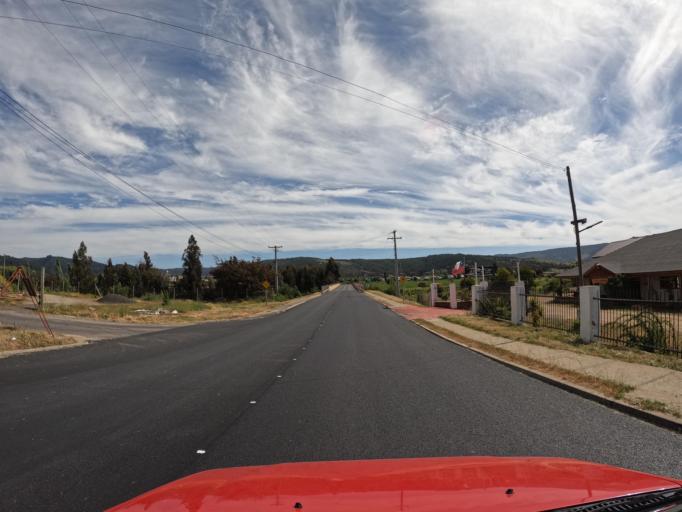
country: CL
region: Maule
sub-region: Provincia de Talca
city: Constitucion
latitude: -35.0852
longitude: -72.0176
